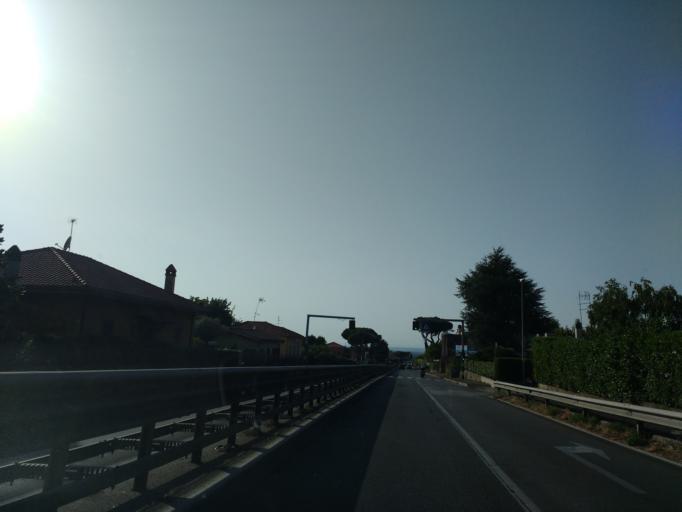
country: IT
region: Latium
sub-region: Citta metropolitana di Roma Capitale
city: Marino
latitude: 41.7612
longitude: 12.6225
